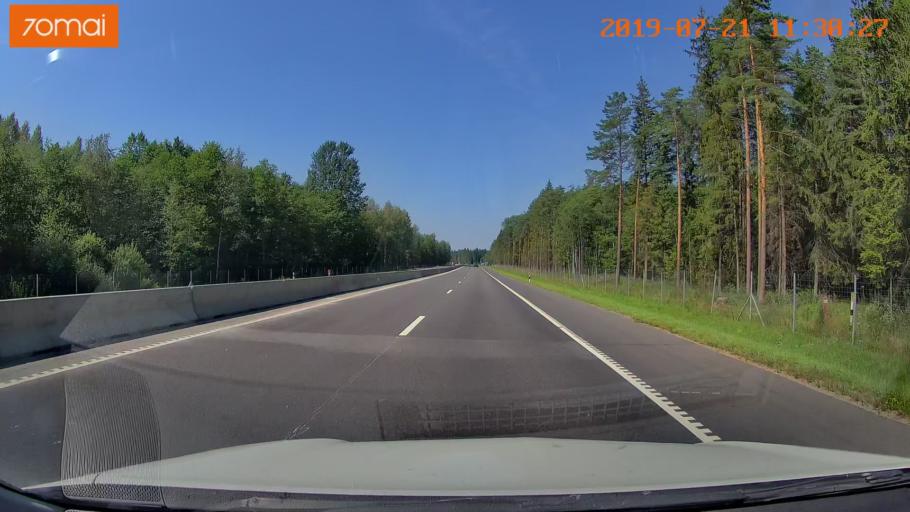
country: BY
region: Minsk
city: Valozhyn
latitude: 54.0216
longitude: 26.4141
